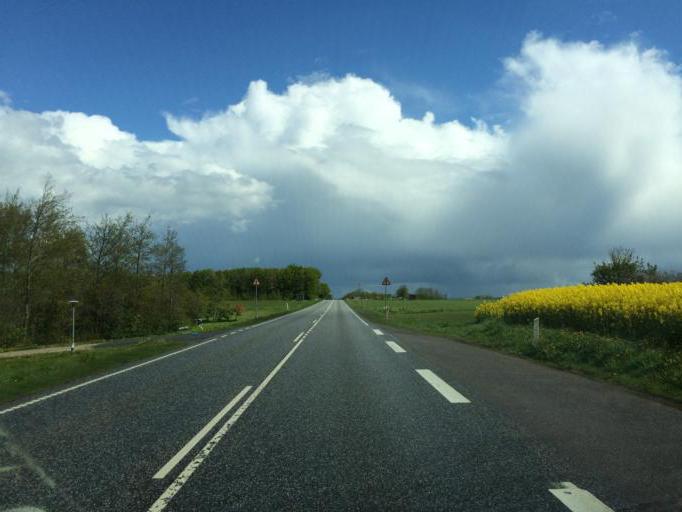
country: DK
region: Central Jutland
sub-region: Holstebro Kommune
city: Holstebro
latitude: 56.4130
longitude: 8.6923
